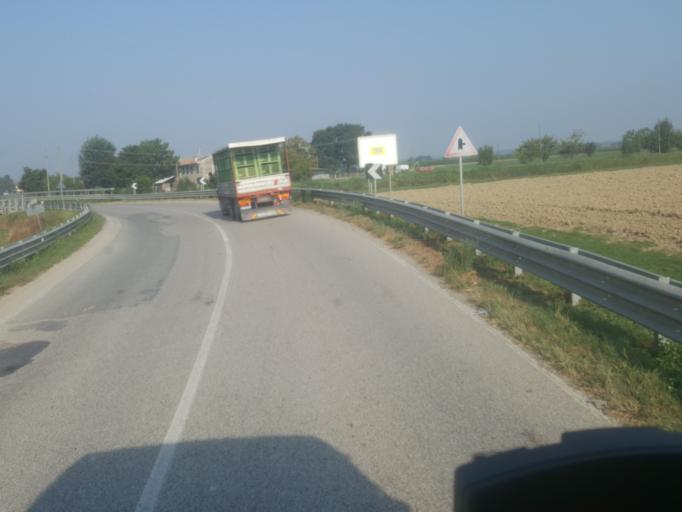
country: IT
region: Emilia-Romagna
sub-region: Provincia di Ferrara
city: Longastrino
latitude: 44.5412
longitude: 11.9911
